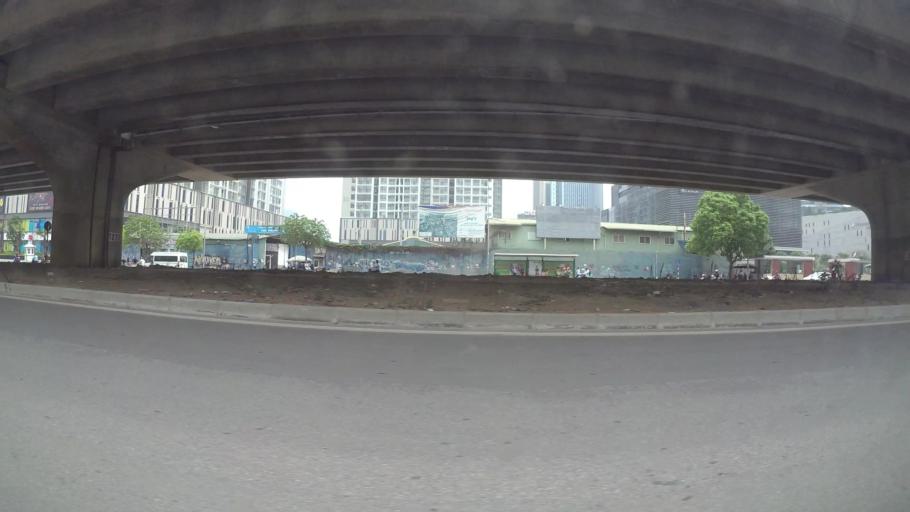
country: VN
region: Ha Noi
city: Cau Giay
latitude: 21.0187
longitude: 105.7813
